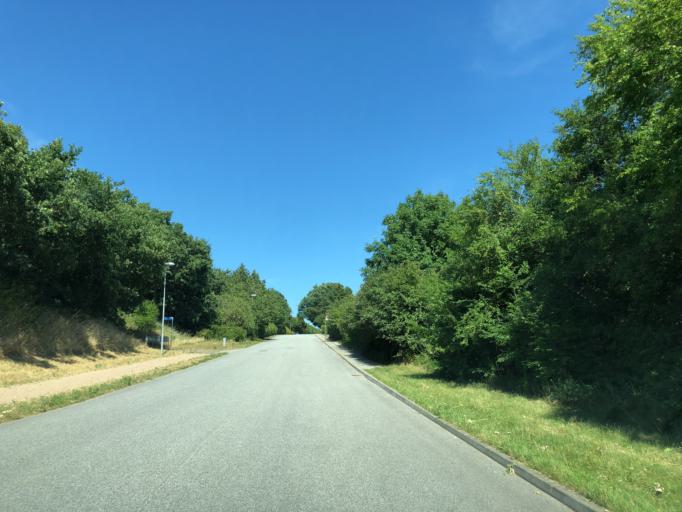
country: DK
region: Central Jutland
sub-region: Skive Kommune
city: Skive
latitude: 56.5472
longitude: 9.0126
